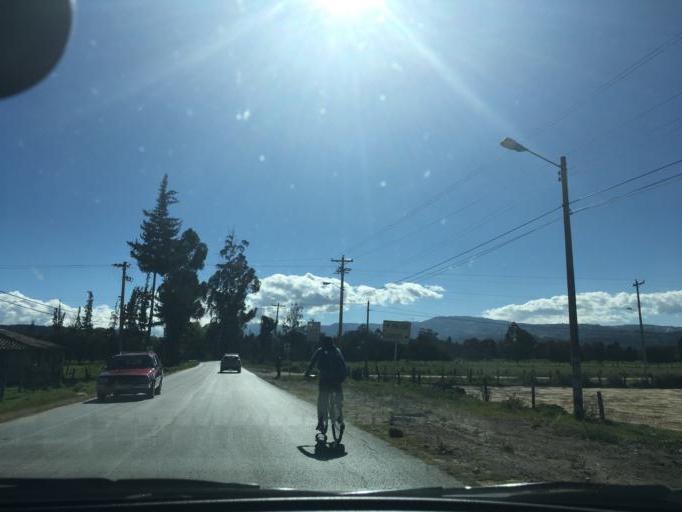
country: CO
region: Boyaca
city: Firavitoba
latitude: 5.6729
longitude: -72.9618
